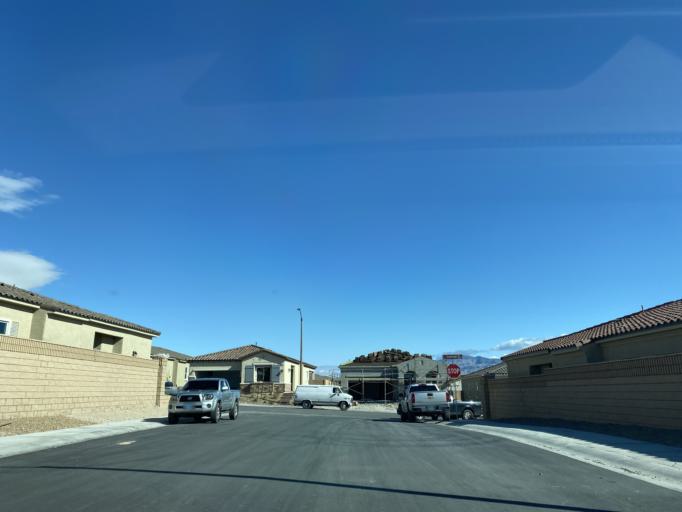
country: US
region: Nevada
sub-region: Clark County
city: Summerlin South
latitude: 36.3092
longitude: -115.3307
